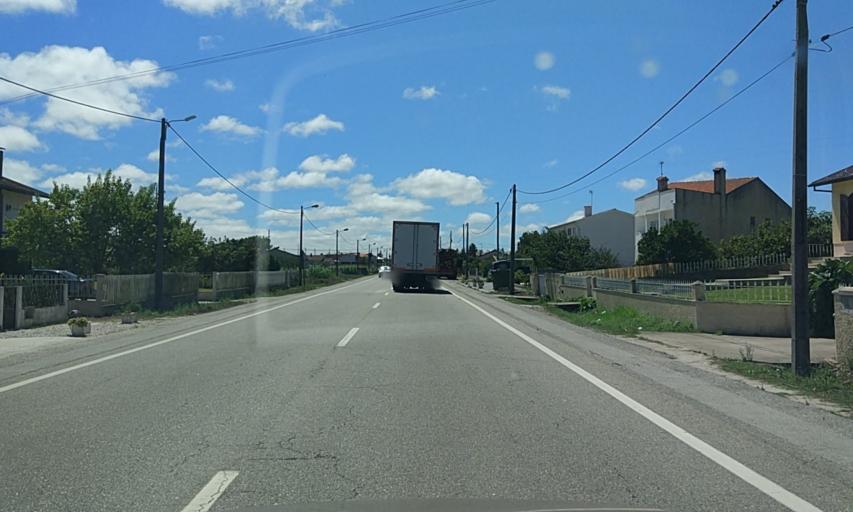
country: PT
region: Coimbra
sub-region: Mira
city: Mira
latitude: 40.4718
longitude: -8.6974
